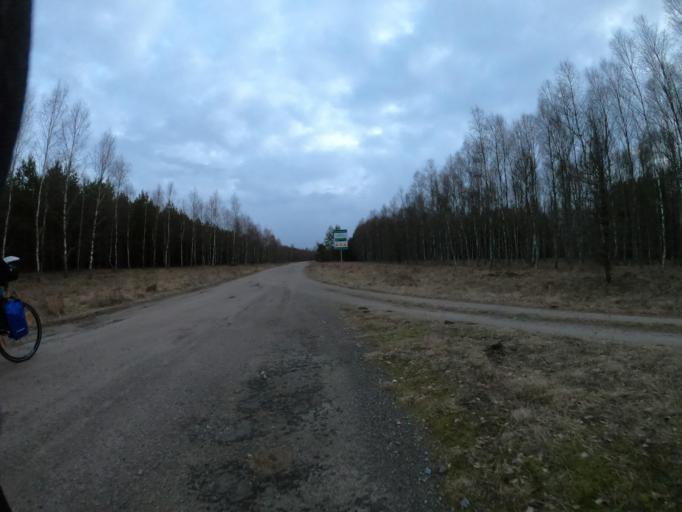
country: PL
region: West Pomeranian Voivodeship
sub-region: Powiat szczecinecki
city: Borne Sulinowo
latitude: 53.5420
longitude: 16.5810
